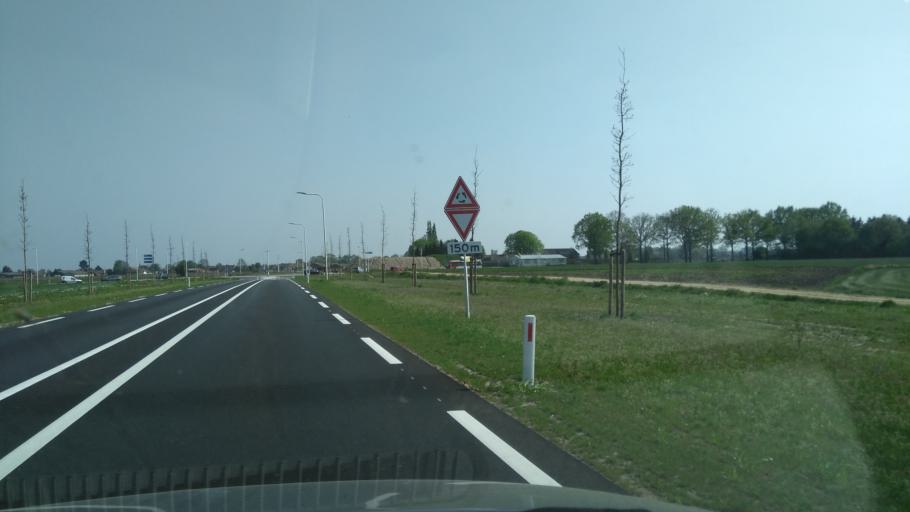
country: NL
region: North Brabant
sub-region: Gemeente Baarle-Nassau
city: Baarle-Nassau
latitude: 51.4541
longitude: 4.9404
